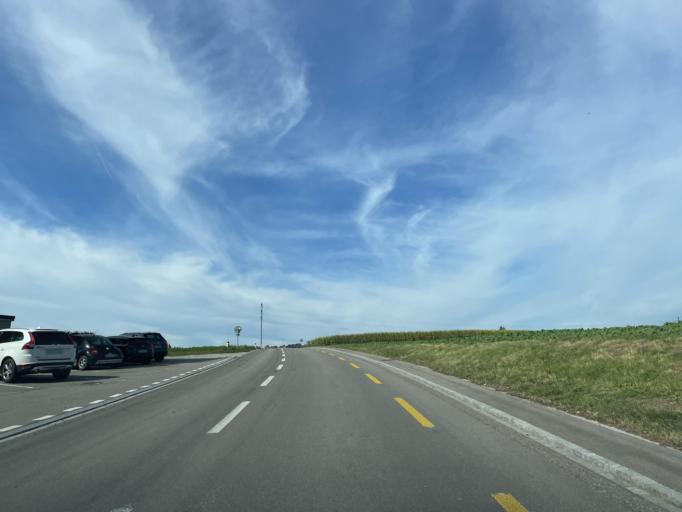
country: CH
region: Zurich
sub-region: Bezirk Winterthur
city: Brutten
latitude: 47.4696
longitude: 8.6867
